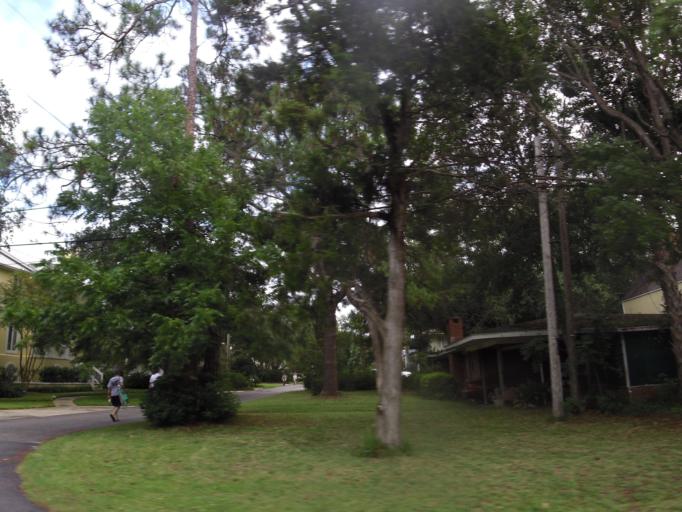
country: US
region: Georgia
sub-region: Glynn County
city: Saint Simons Island
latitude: 31.1505
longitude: -81.3699
